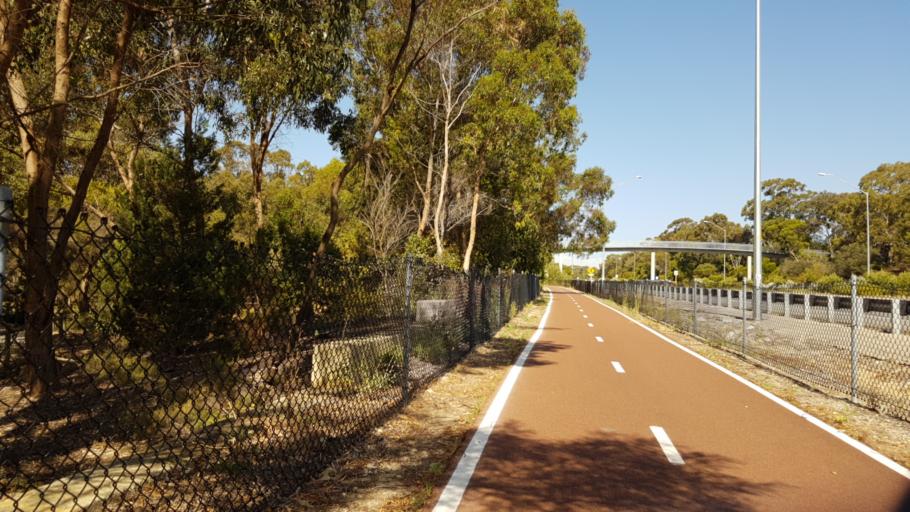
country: AU
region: Western Australia
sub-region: Stirling
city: Karrinyup
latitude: -31.8566
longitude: 115.7865
